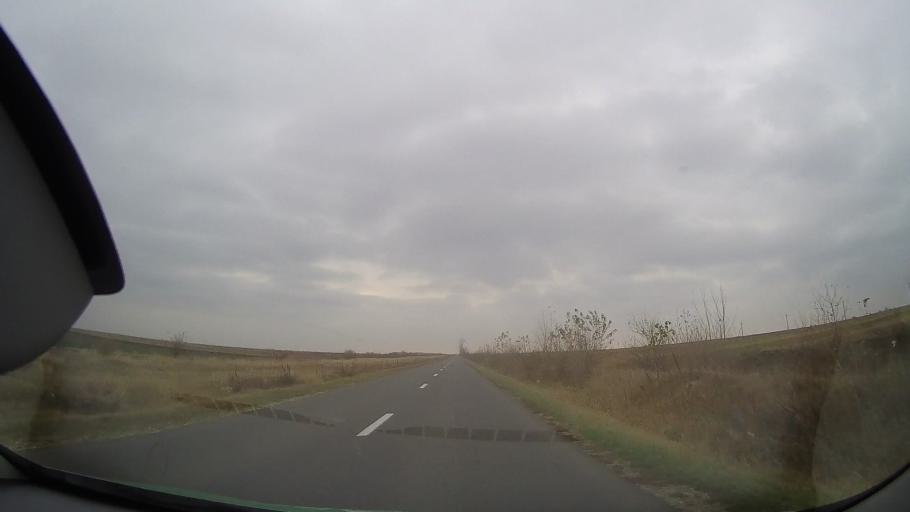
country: RO
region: Ialomita
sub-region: Comuna Garbovi
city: Garbovi
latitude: 44.7661
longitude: 26.7384
